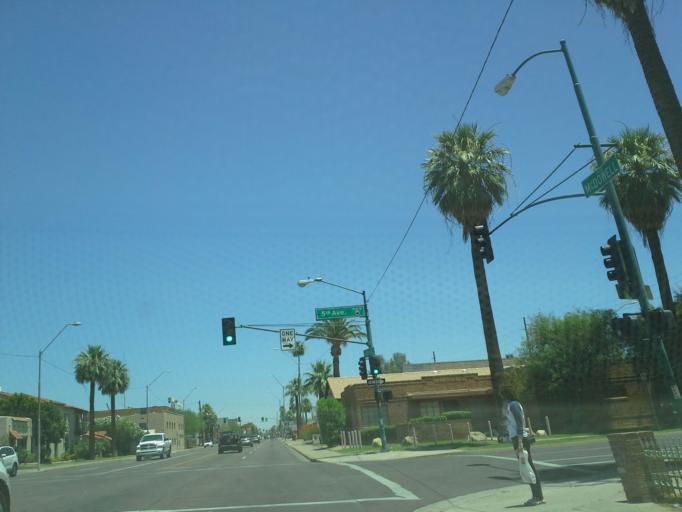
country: US
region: Arizona
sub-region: Maricopa County
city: Phoenix
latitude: 33.4658
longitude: -112.0805
